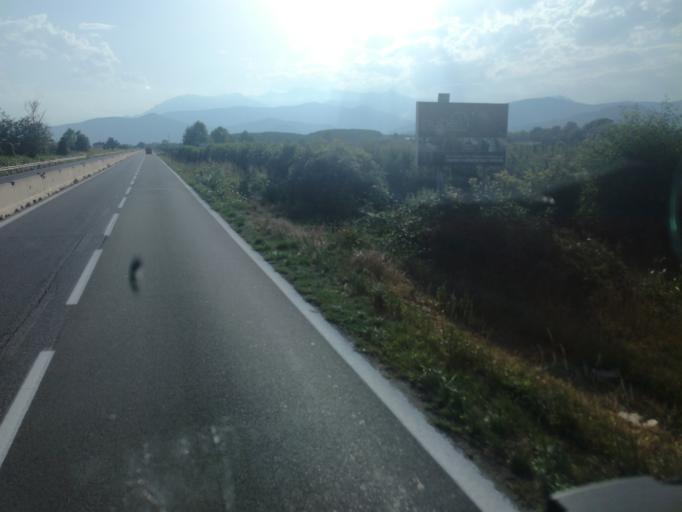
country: IT
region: Piedmont
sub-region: Provincia di Torino
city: Riva
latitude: 44.8881
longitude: 7.3811
